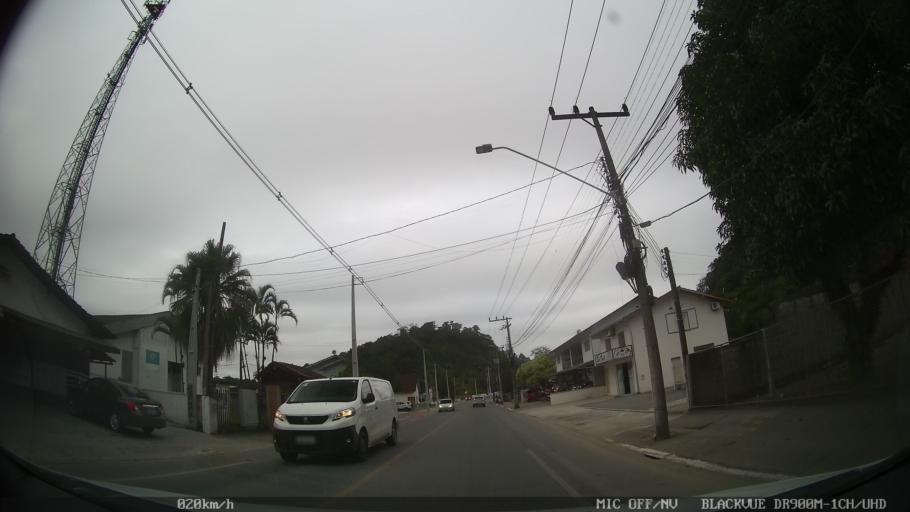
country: BR
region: Santa Catarina
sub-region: Joinville
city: Joinville
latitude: -26.2109
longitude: -48.9063
